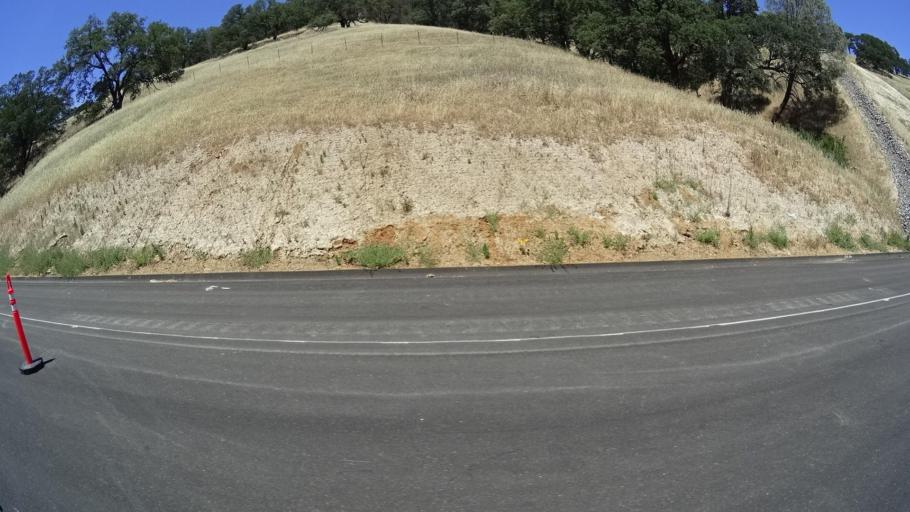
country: US
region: California
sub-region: Lake County
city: Hidden Valley Lake
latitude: 38.8401
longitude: -122.5934
